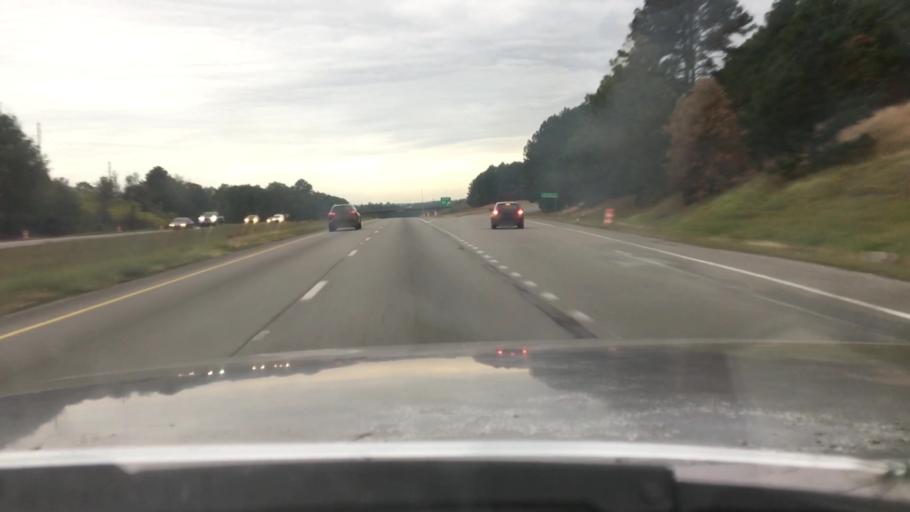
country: US
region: South Carolina
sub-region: Lexington County
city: Red Bank
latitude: 33.9298
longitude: -81.2860
